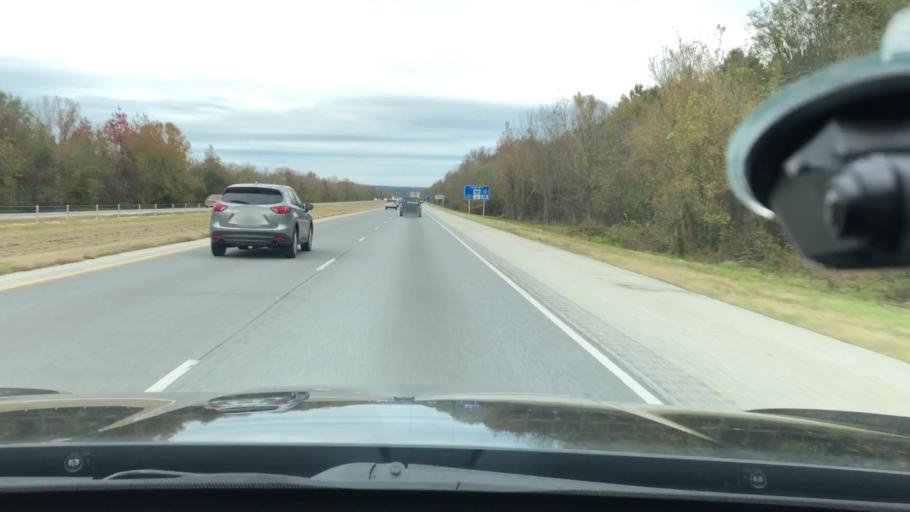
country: US
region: Arkansas
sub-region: Clark County
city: Arkadelphia
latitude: 34.1576
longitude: -93.0773
